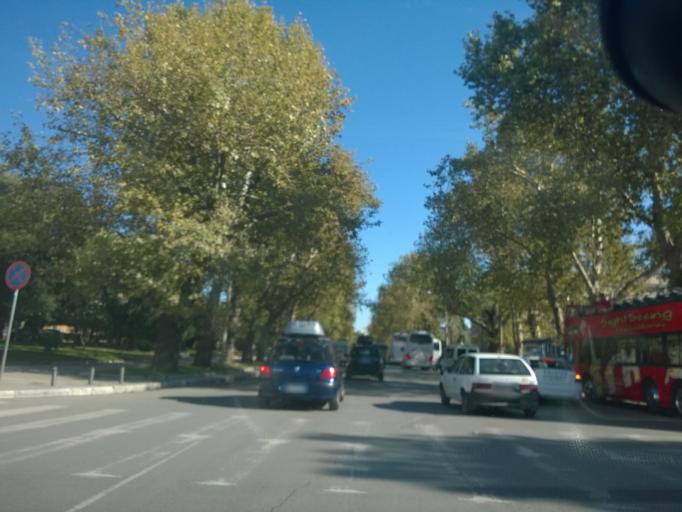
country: GR
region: Central Macedonia
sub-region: Nomos Thessalonikis
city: Agios Pavlos
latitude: 40.6260
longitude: 22.9494
